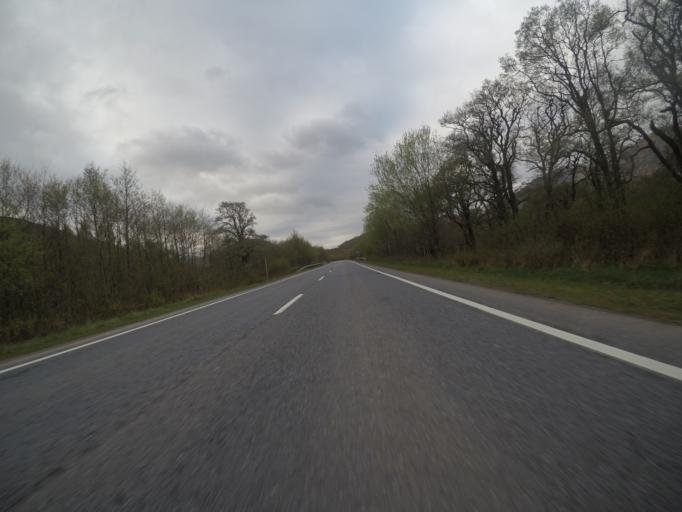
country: GB
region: Scotland
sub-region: Highland
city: Spean Bridge
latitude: 56.9500
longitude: -4.4976
